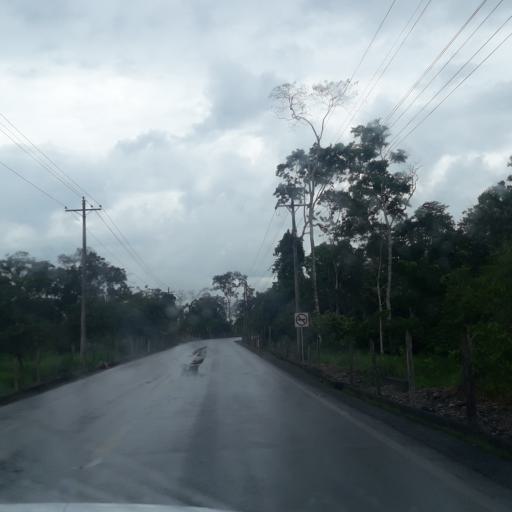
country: EC
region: Napo
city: Tena
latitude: -1.0658
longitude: -77.6490
